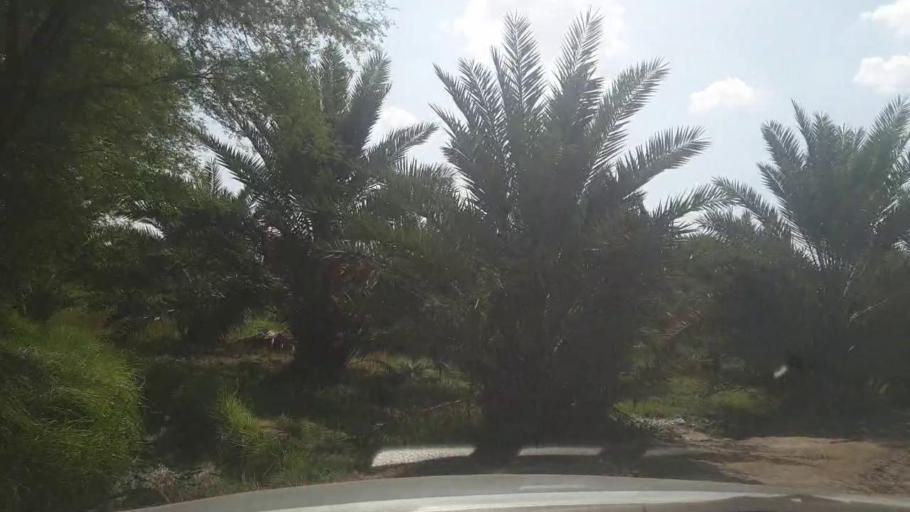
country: PK
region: Sindh
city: Khairpur
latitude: 27.5516
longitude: 68.8079
